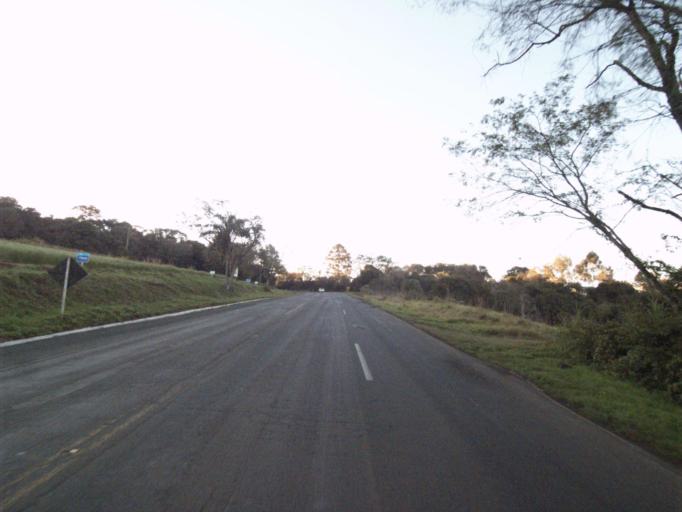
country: BR
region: Santa Catarina
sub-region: Sao Lourenco Do Oeste
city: Sao Lourenco dOeste
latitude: -26.8114
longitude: -53.1676
